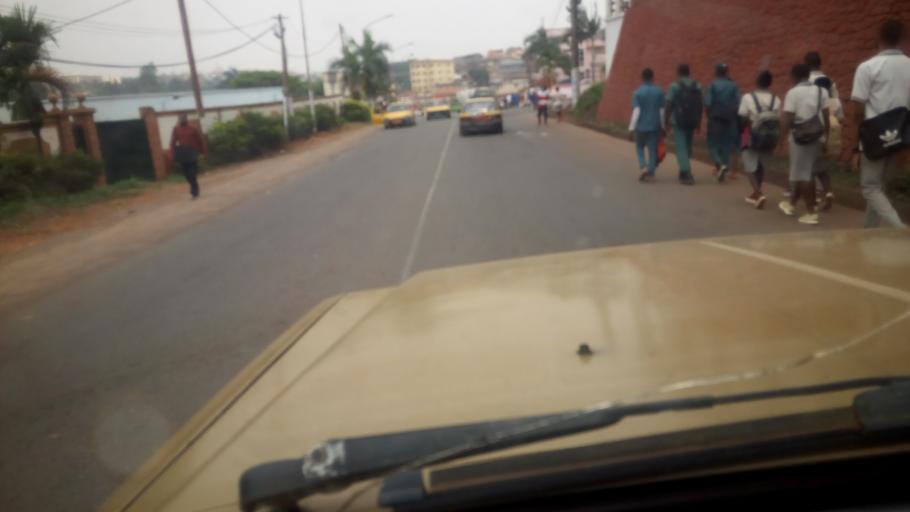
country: CM
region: Centre
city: Yaounde
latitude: 3.8556
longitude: 11.5193
